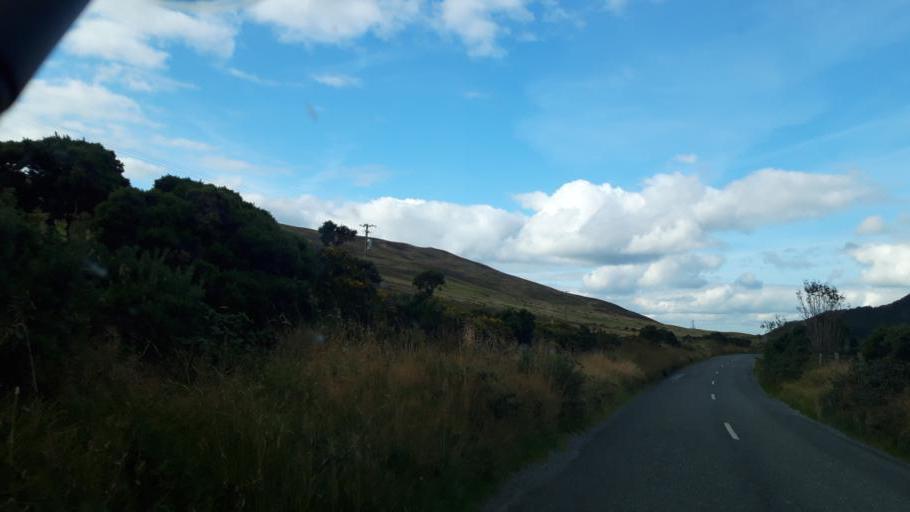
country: GB
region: Northern Ireland
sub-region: Down District
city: Warrenpoint
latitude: 54.0437
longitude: -6.2695
